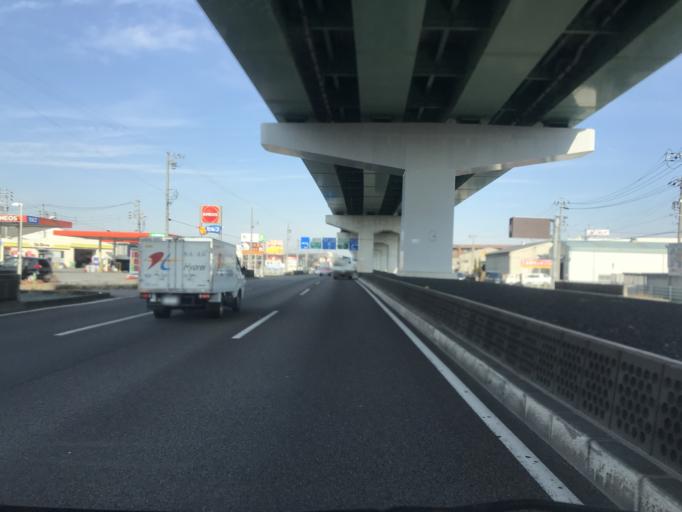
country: JP
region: Aichi
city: Iwakura
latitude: 35.2260
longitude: 136.8531
